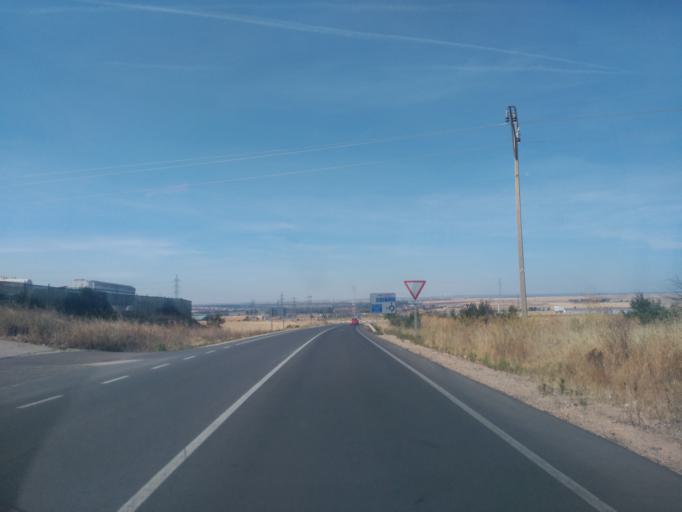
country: ES
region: Castille and Leon
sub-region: Provincia de Salamanca
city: Villamayor
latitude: 40.9843
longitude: -5.6821
